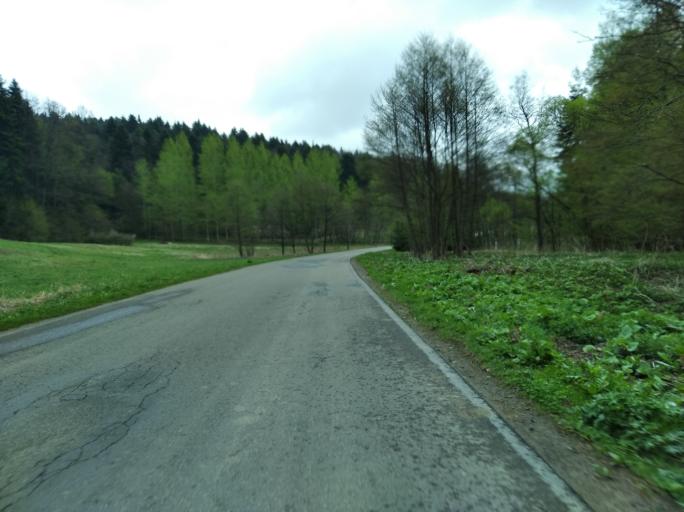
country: PL
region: Subcarpathian Voivodeship
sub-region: Powiat brzozowski
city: Golcowa
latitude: 49.7452
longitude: 22.0756
